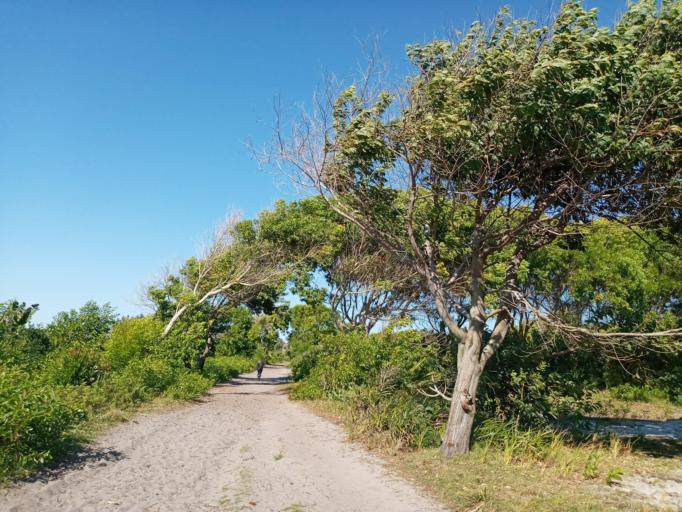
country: MG
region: Anosy
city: Fort Dauphin
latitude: -24.9068
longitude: 47.1027
